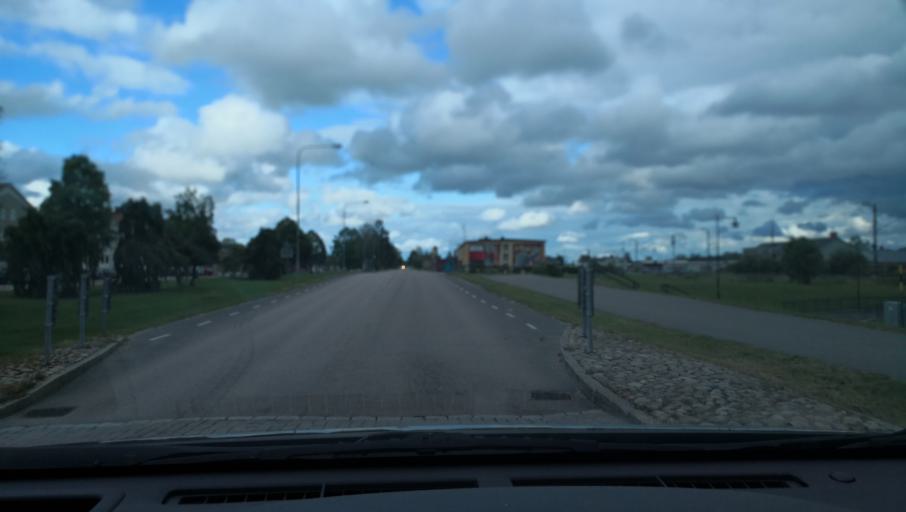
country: SE
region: Vaestmanland
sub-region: Arboga Kommun
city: Arboga
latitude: 59.3984
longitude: 15.8580
